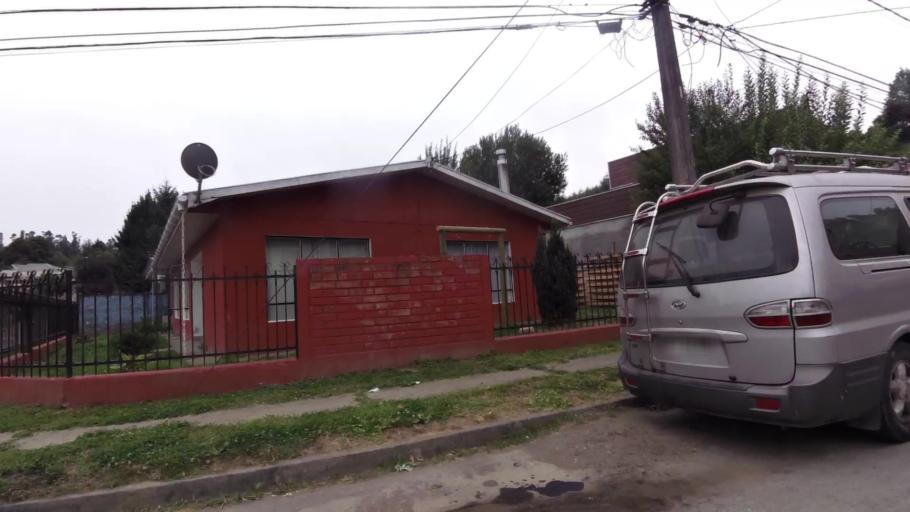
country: CL
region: Biobio
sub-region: Provincia de Concepcion
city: Concepcion
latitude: -36.8251
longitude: -73.0064
